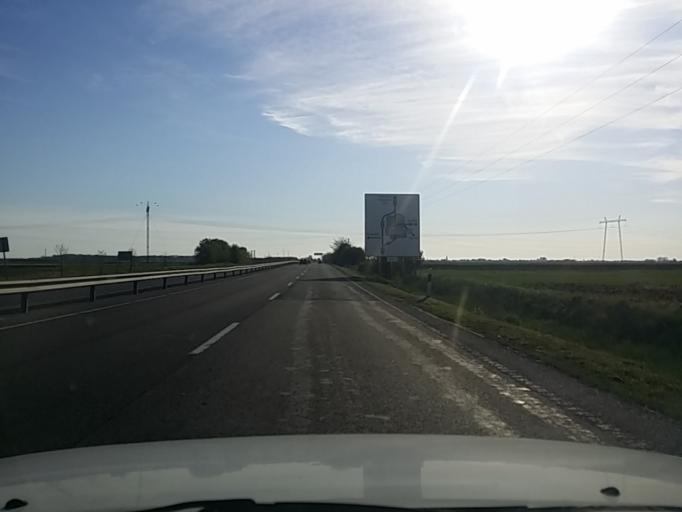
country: HU
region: Jasz-Nagykun-Szolnok
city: Szajol
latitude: 47.1804
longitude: 20.3430
